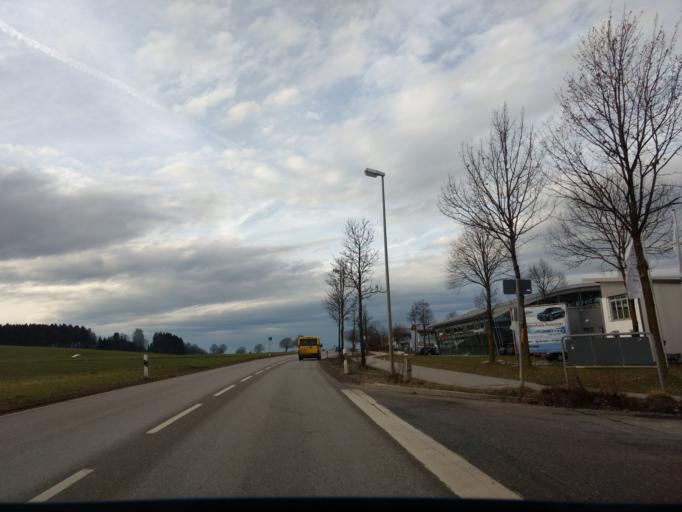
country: DE
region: Bavaria
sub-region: Upper Bavaria
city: Vachendorf
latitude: 47.8692
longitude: 12.6172
